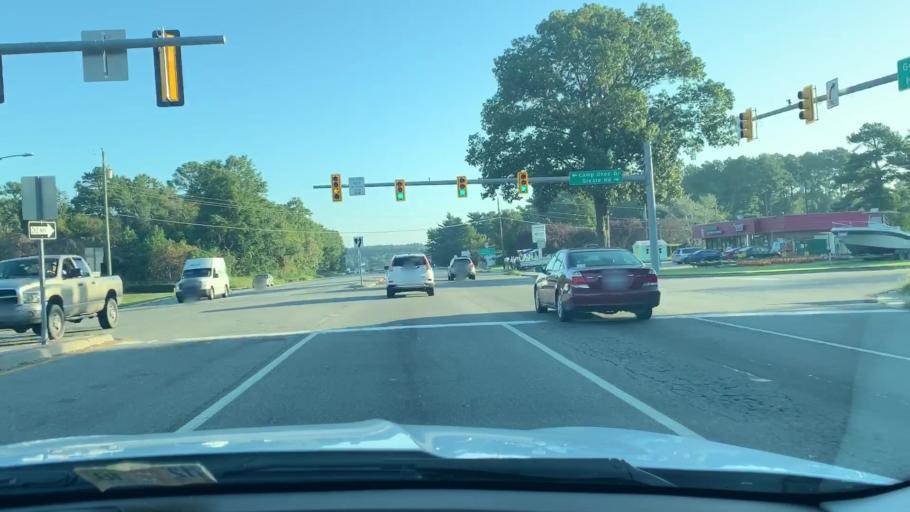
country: US
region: Virginia
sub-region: Gloucester County
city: Gloucester Point
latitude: 37.2556
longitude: -76.4970
